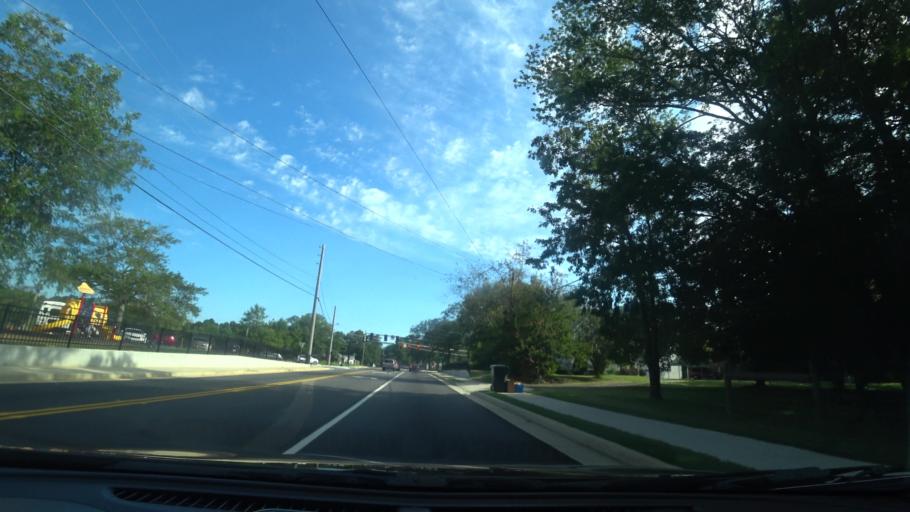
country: US
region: Georgia
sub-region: Gwinnett County
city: Grayson
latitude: 33.8915
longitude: -83.9603
